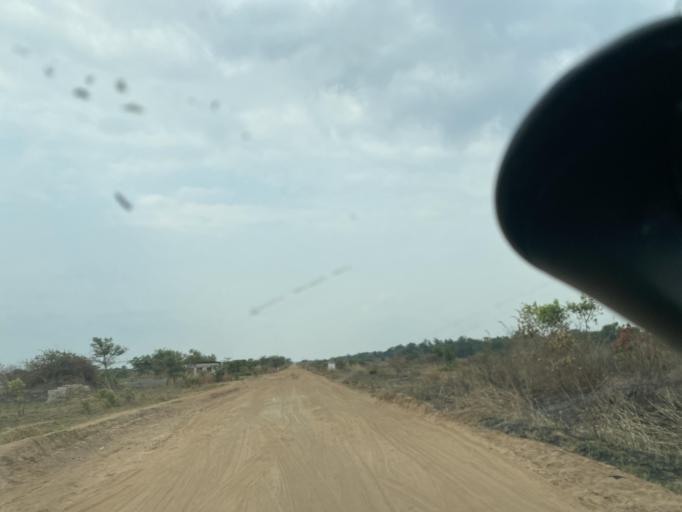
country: ZM
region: Lusaka
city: Lusaka
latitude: -15.2103
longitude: 28.3395
